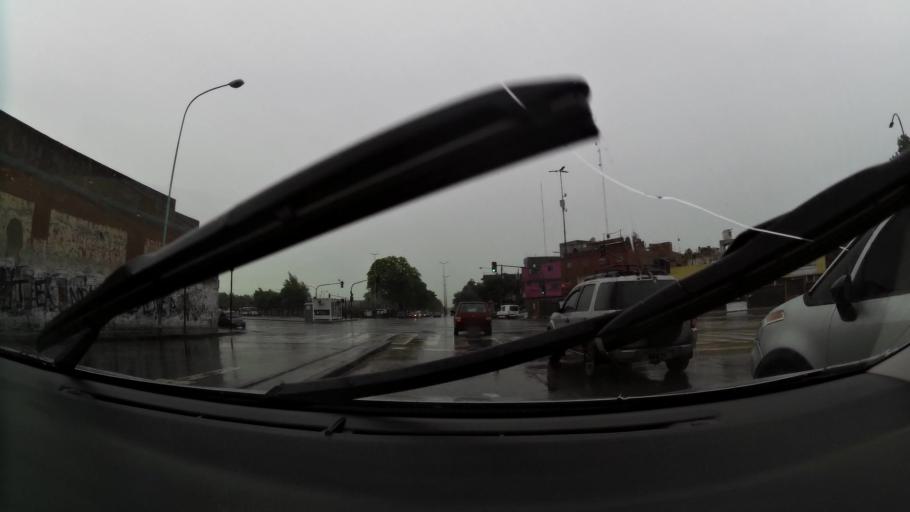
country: AR
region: Buenos Aires F.D.
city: Villa Lugano
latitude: -34.6503
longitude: -58.4306
